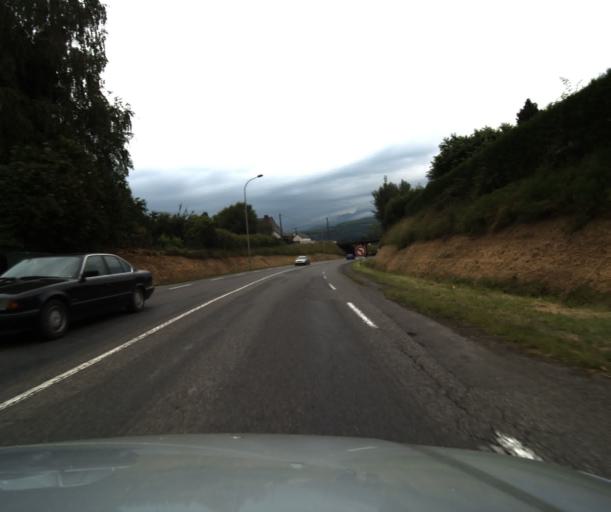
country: FR
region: Midi-Pyrenees
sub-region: Departement des Hautes-Pyrenees
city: Lourdes
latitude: 43.1035
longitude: -0.0307
